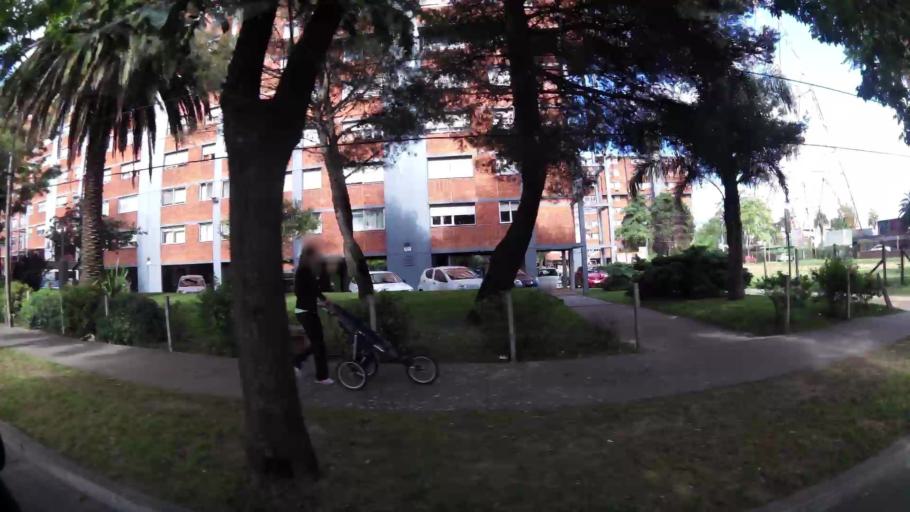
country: UY
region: Montevideo
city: Montevideo
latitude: -34.8796
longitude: -56.1653
